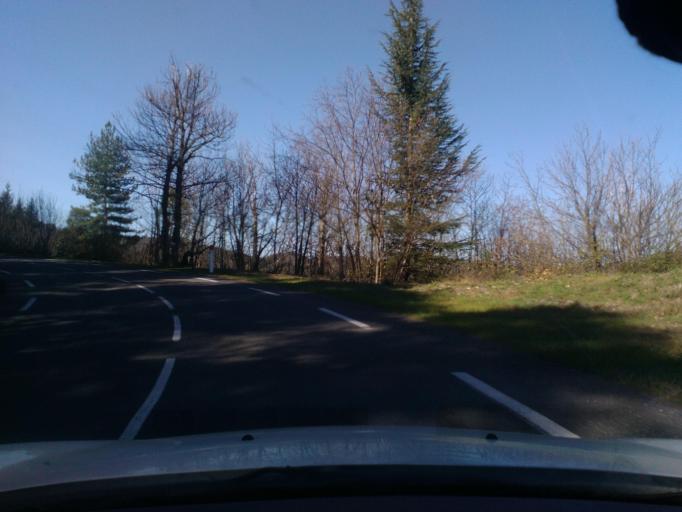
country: FR
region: Languedoc-Roussillon
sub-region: Departement du Gard
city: Saint-Jean-du-Gard
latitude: 44.1378
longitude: 3.8223
